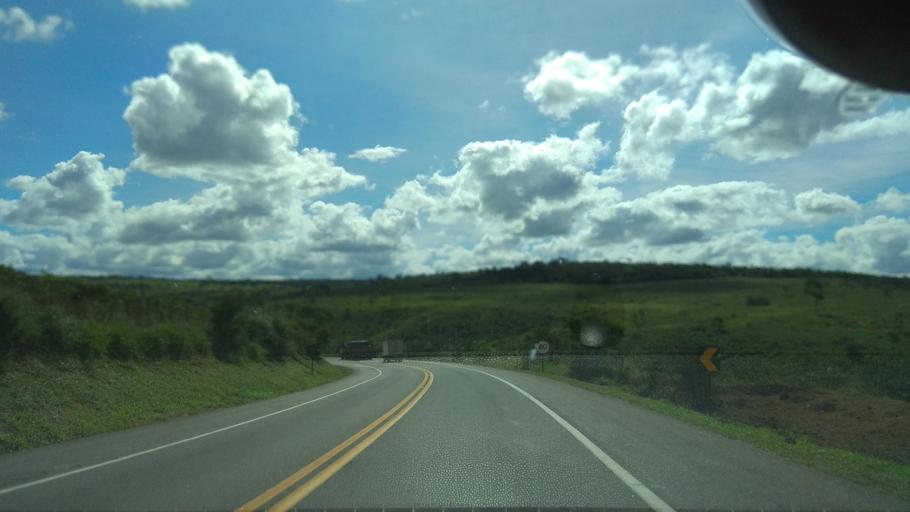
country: BR
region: Bahia
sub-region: Santa Ines
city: Santa Ines
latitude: -13.2263
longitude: -40.0193
